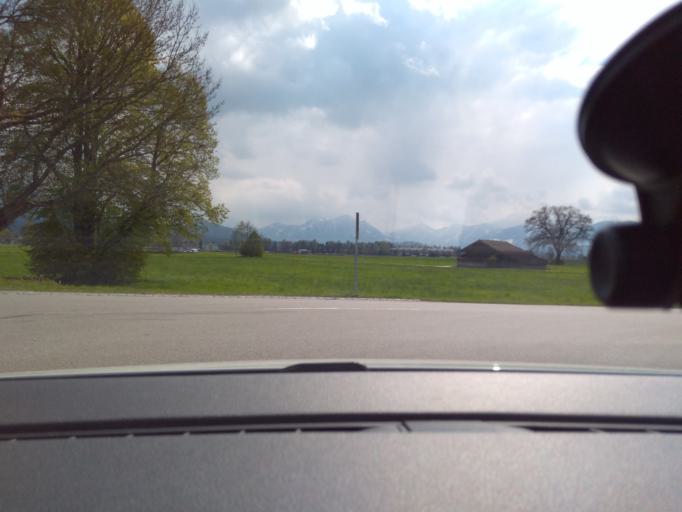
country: DE
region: Bavaria
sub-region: Upper Bavaria
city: Rohrdorf
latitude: 47.8091
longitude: 12.1617
